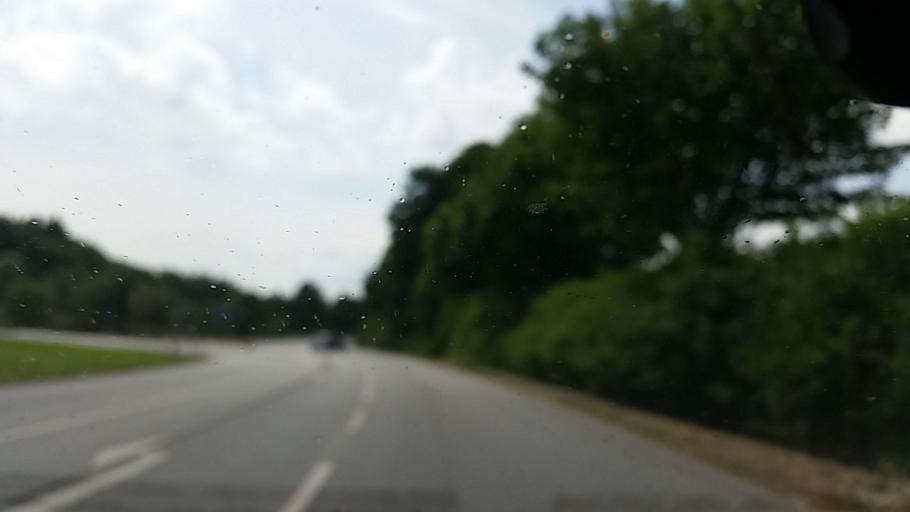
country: DE
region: Schleswig-Holstein
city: Grabau
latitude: 53.7930
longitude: 10.3142
